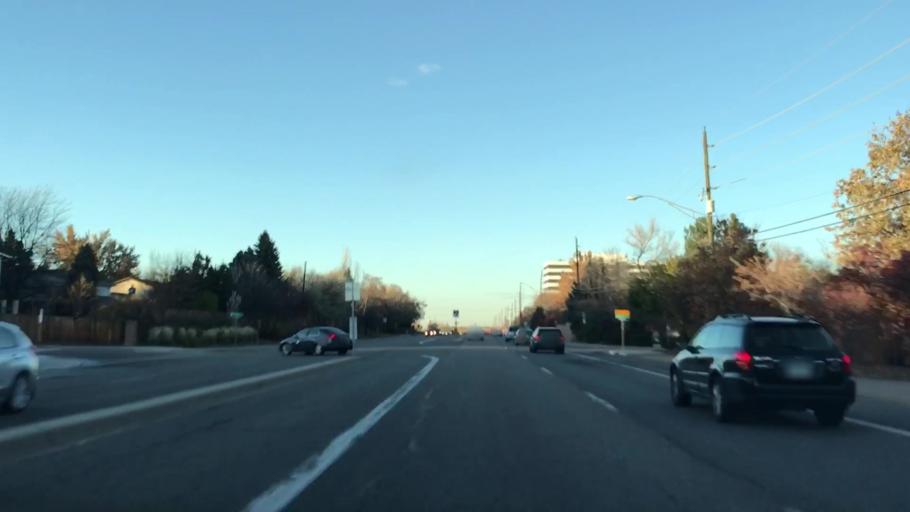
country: US
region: Colorado
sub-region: Arapahoe County
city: Castlewood
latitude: 39.6472
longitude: -104.8850
